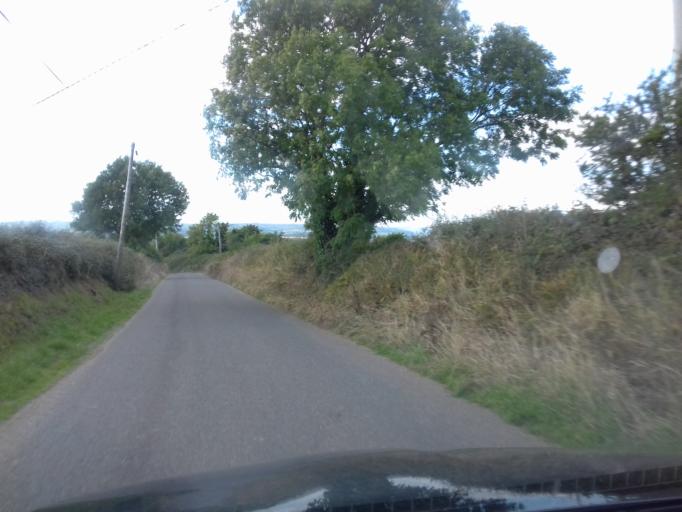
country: IE
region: Leinster
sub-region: Kilkenny
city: Graiguenamanagh
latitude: 52.5769
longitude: -7.0093
